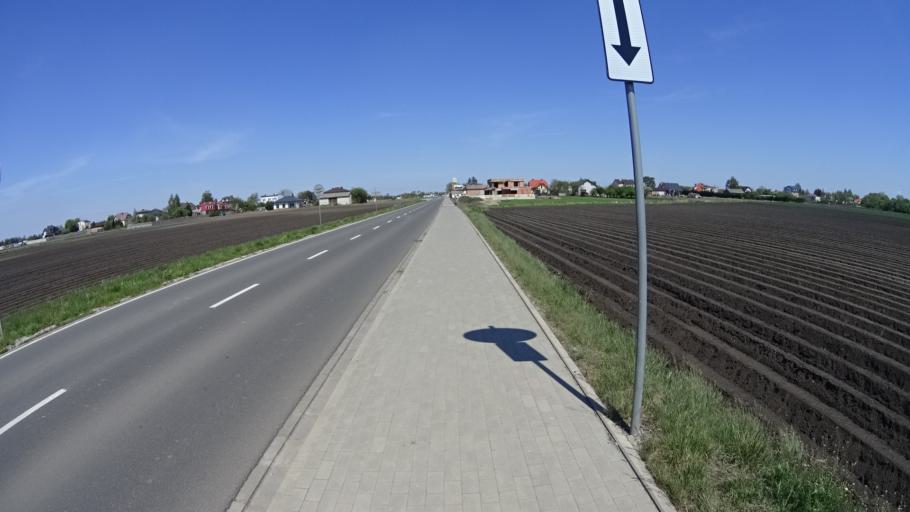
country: PL
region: Masovian Voivodeship
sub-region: Powiat warszawski zachodni
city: Jozefow
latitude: 52.2382
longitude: 20.7378
